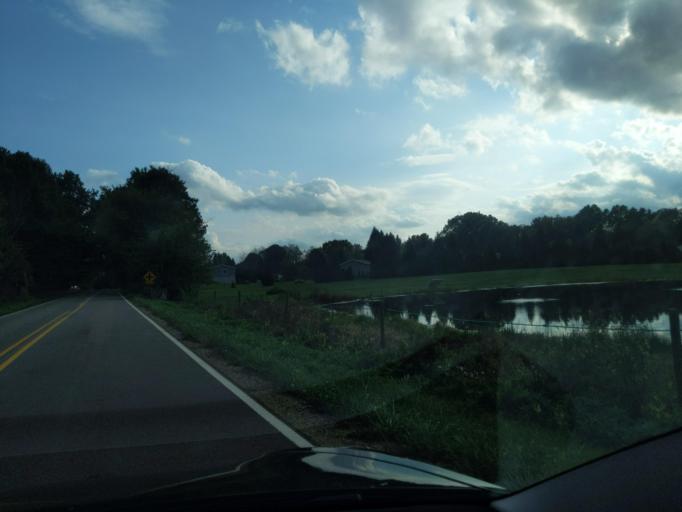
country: US
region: Michigan
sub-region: Ingham County
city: Leslie
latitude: 42.3782
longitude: -84.4432
